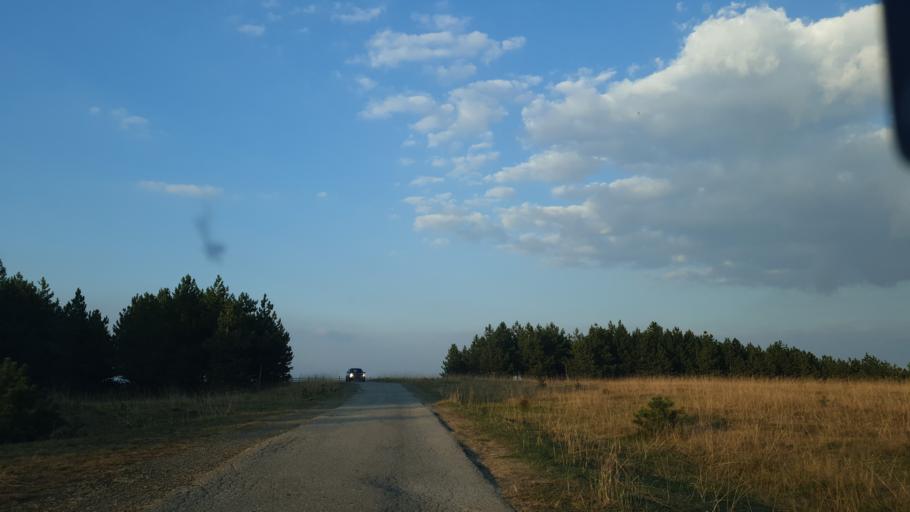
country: RS
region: Central Serbia
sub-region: Zlatiborski Okrug
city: Kosjeric
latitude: 44.0194
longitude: 20.0025
